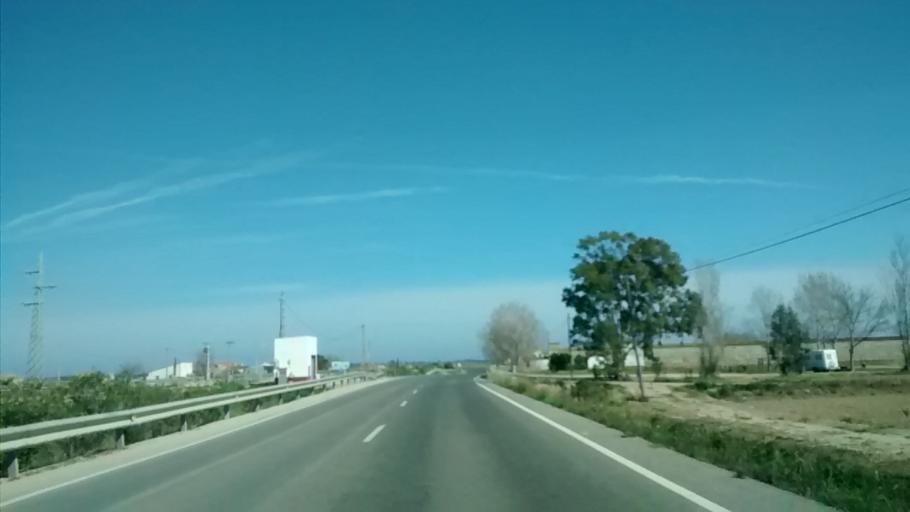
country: ES
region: Catalonia
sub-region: Provincia de Tarragona
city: Deltebre
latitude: 40.7050
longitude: 0.7852
